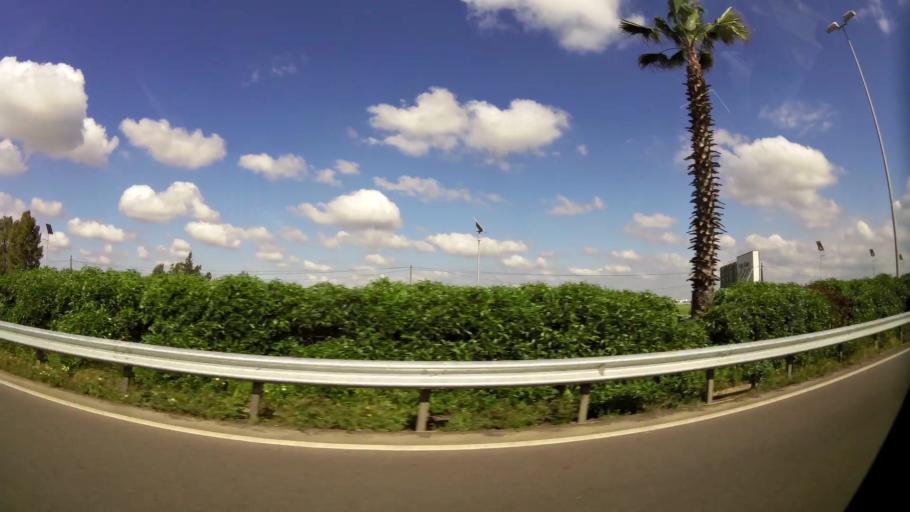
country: MA
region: Chaouia-Ouardigha
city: Nouaseur
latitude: 33.4096
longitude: -7.6260
